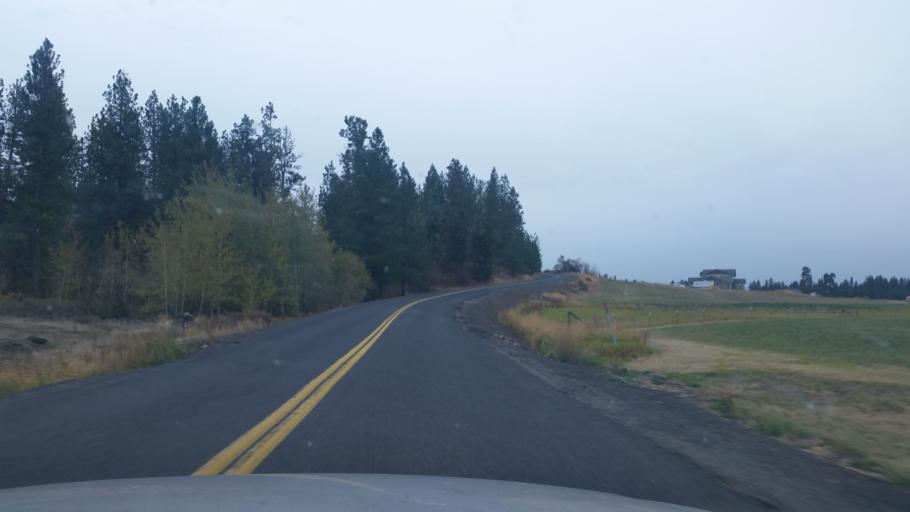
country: US
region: Washington
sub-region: Spokane County
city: Cheney
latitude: 47.5361
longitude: -117.5511
